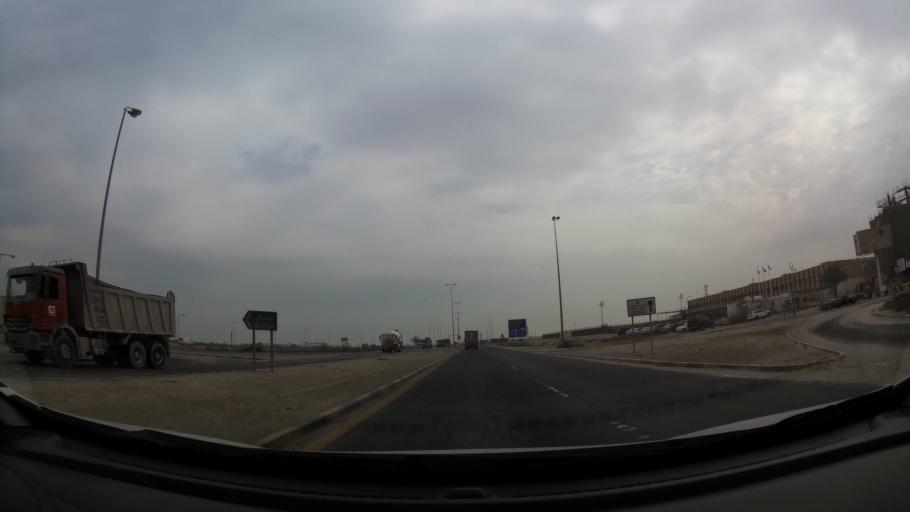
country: BH
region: Northern
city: Sitrah
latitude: 26.0772
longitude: 50.6139
